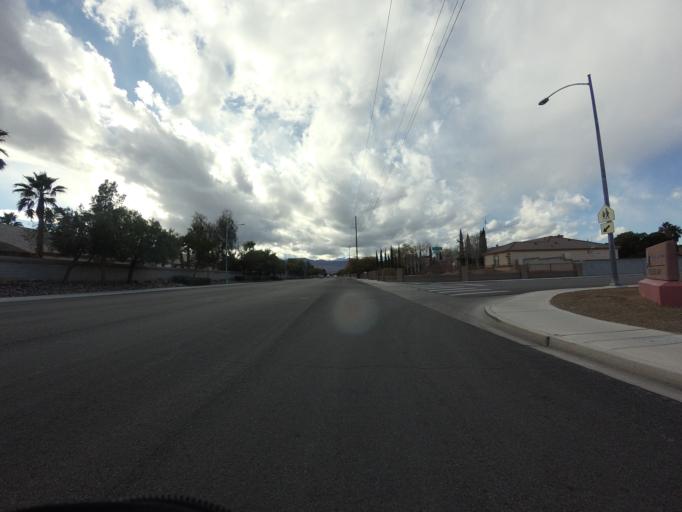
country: US
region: Nevada
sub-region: Clark County
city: Las Vegas
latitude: 36.2695
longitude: -115.2401
